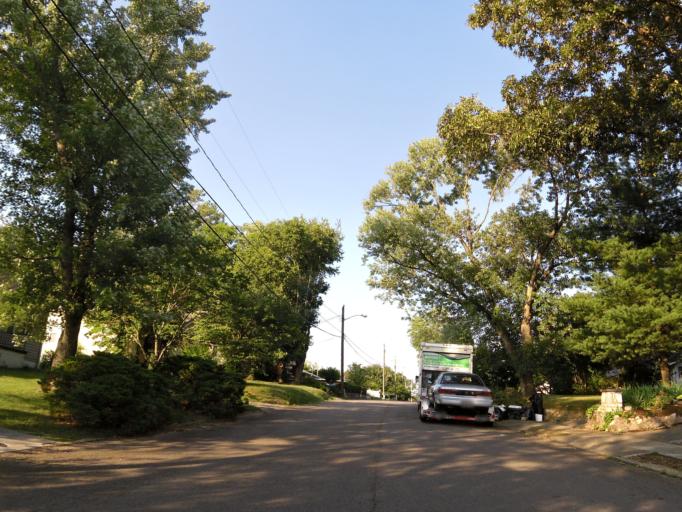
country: US
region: Tennessee
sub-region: Knox County
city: Knoxville
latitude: 36.0342
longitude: -83.9249
